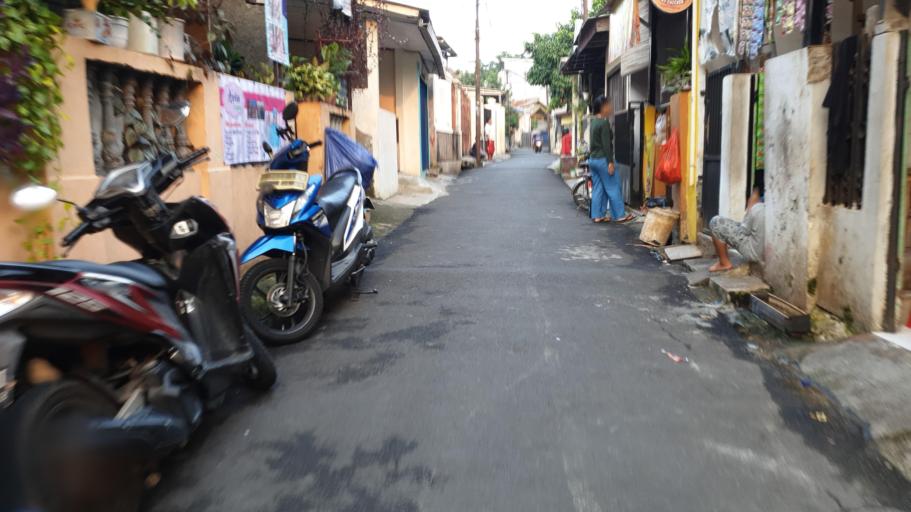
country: ID
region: West Java
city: Depok
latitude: -6.3280
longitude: 106.8323
